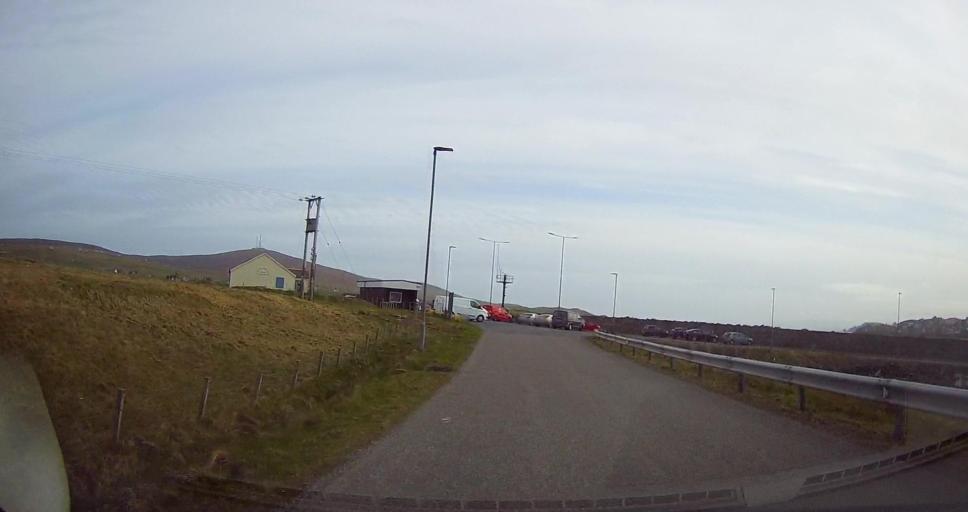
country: GB
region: Scotland
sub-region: Shetland Islands
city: Shetland
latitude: 60.1569
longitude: -1.1213
